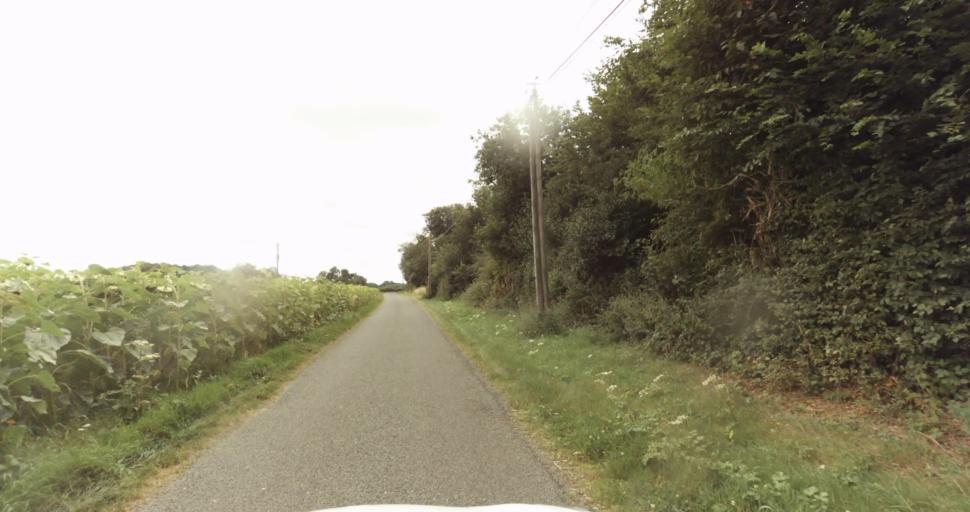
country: FR
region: Haute-Normandie
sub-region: Departement de l'Eure
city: Saint-Germain-sur-Avre
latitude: 48.8279
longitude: 1.2550
